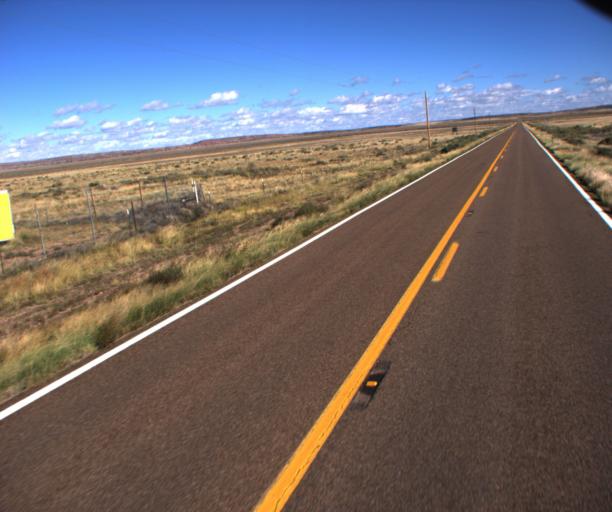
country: US
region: Arizona
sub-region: Apache County
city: Saint Johns
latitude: 34.5979
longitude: -109.3257
